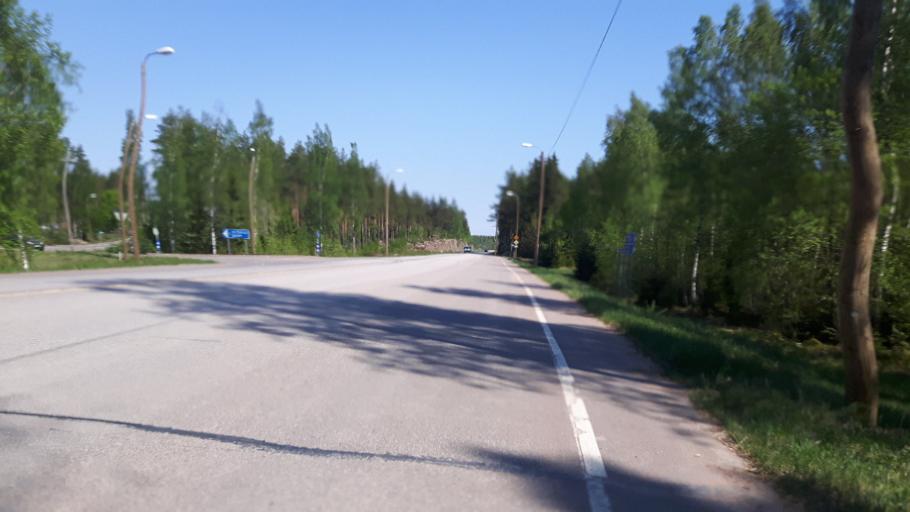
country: FI
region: Kymenlaakso
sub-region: Kotka-Hamina
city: Broby
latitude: 60.4906
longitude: 26.6897
